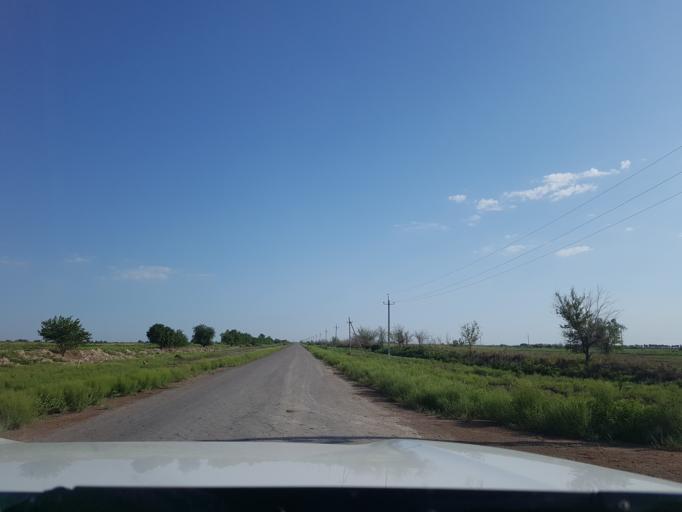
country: TM
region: Dasoguz
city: Koeneuergench
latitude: 41.8493
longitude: 58.7048
